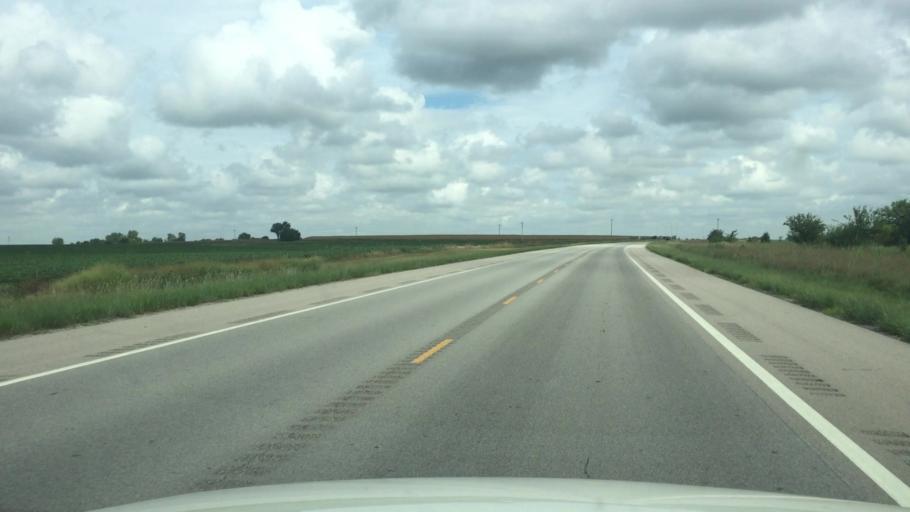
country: US
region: Kansas
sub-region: Allen County
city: Iola
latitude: 37.9467
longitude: -95.3805
